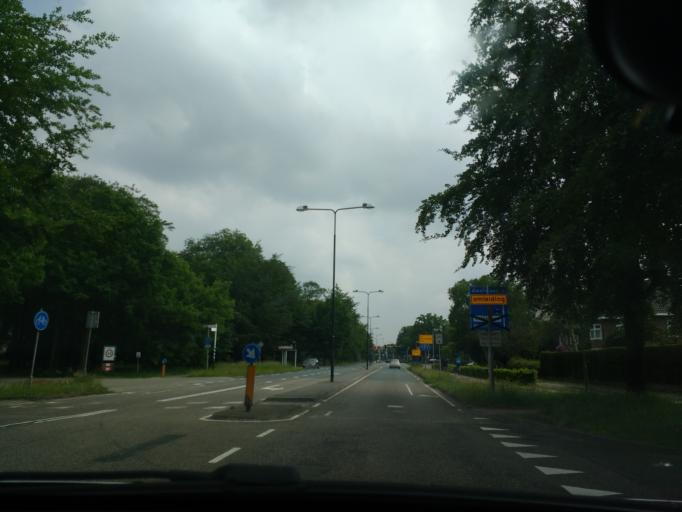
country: NL
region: North Holland
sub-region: Gemeente Naarden
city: Naarden
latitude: 52.2846
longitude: 5.1773
